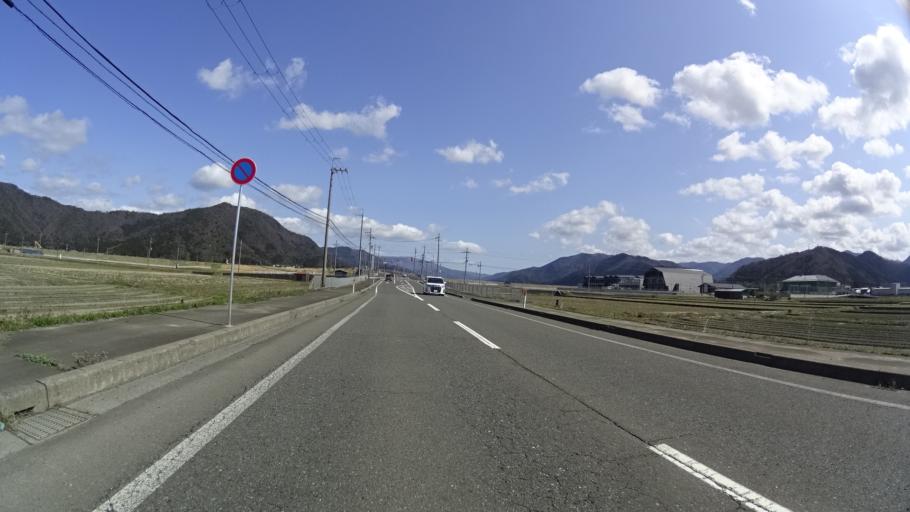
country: JP
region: Fukui
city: Obama
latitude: 35.4875
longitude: 135.7834
